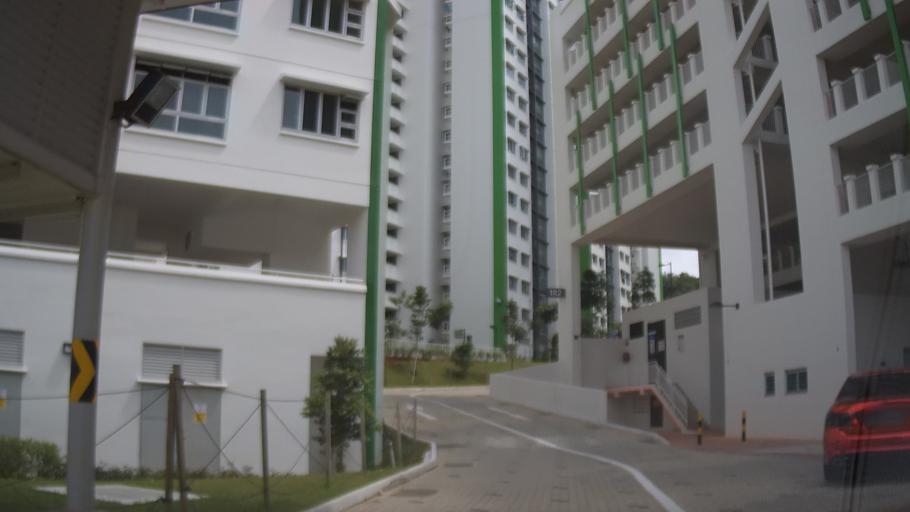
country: MY
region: Johor
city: Johor Bahru
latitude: 1.4355
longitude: 103.7756
